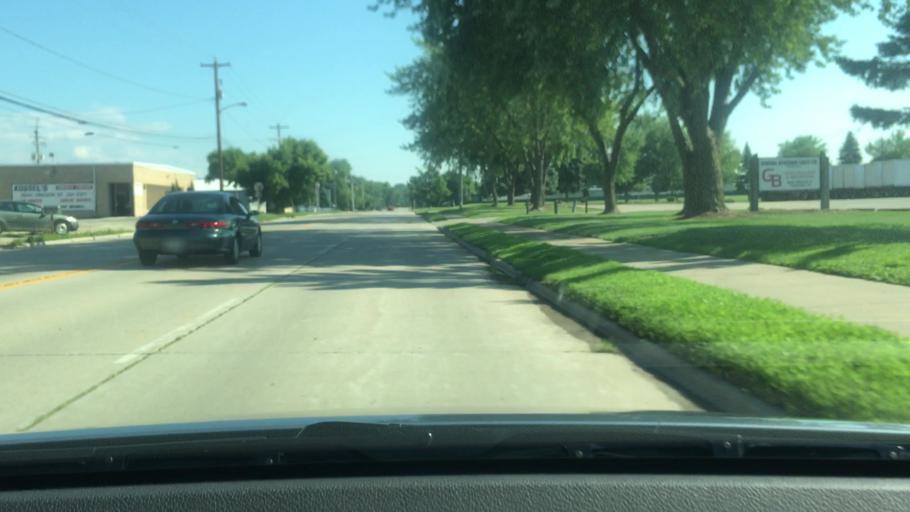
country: US
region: Wisconsin
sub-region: Winnebago County
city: Oshkosh
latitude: 43.9854
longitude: -88.5426
